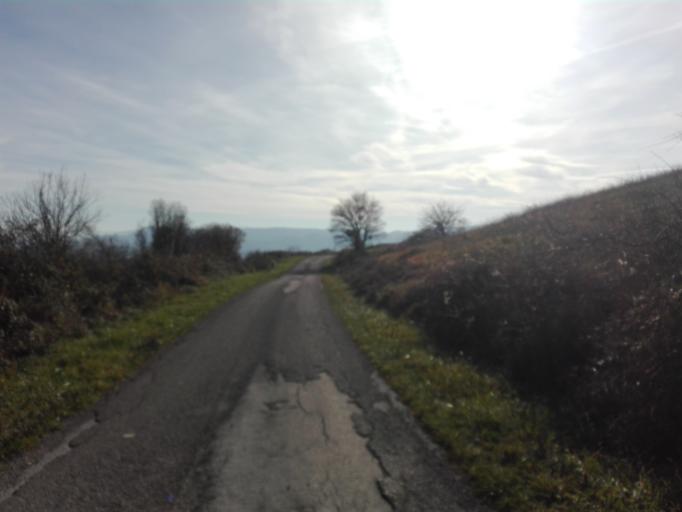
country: IT
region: Molise
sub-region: Provincia di Isernia
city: Agnone
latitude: 41.8505
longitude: 14.3542
